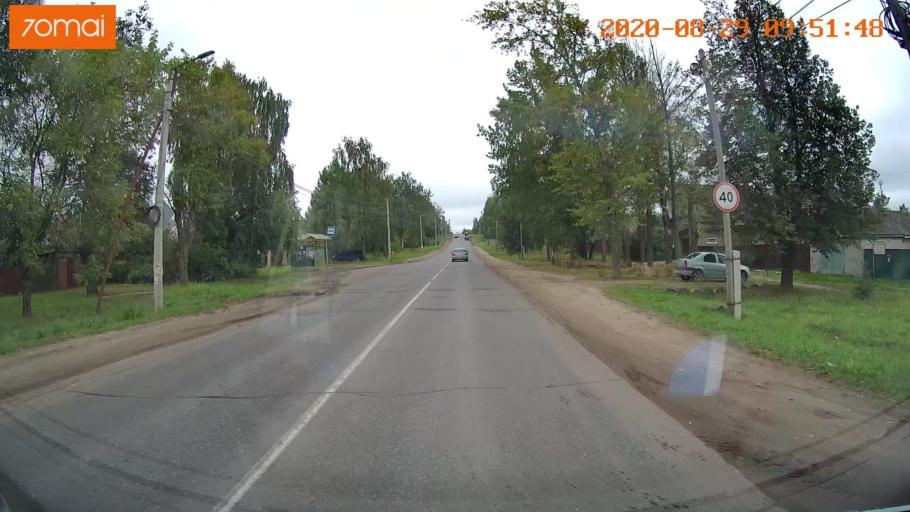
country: RU
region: Ivanovo
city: Kineshma
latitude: 57.4276
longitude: 42.2018
